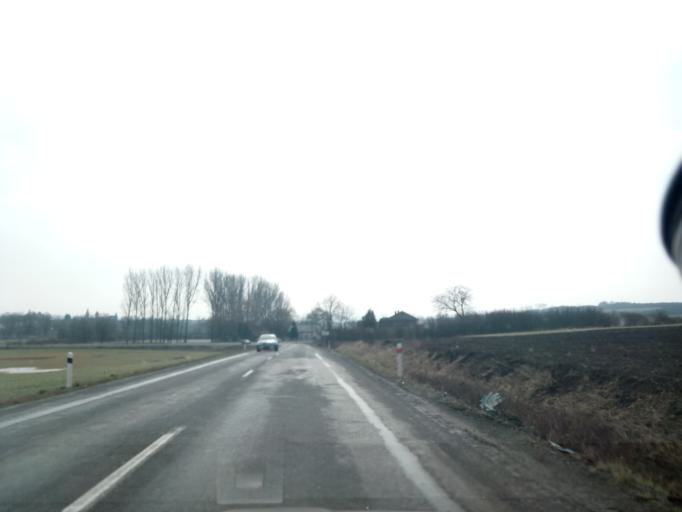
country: SK
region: Kosicky
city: Secovce
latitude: 48.6086
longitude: 21.6179
